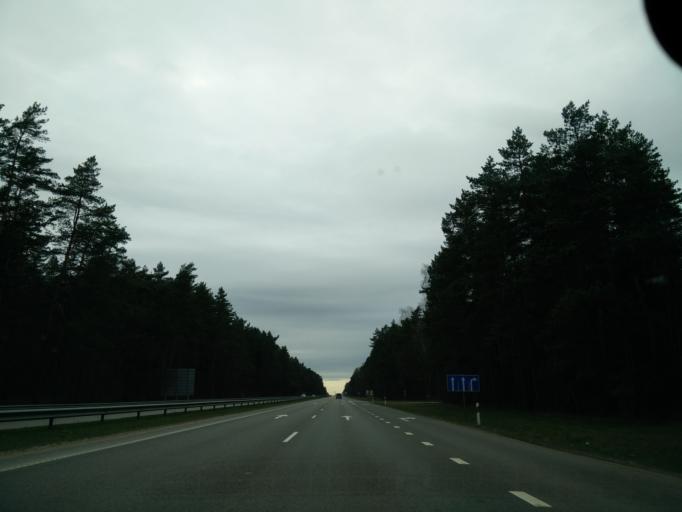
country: LT
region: Vilnius County
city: Lazdynai
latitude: 54.6454
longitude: 25.1729
